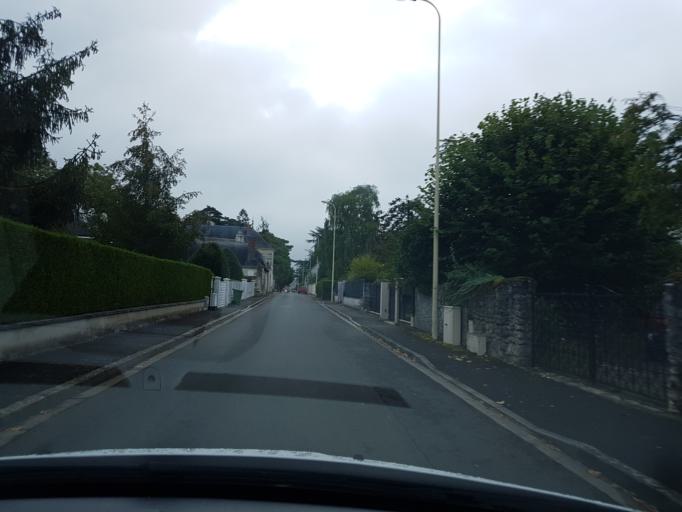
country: FR
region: Centre
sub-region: Departement d'Indre-et-Loire
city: Saint-Avertin
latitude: 47.3670
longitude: 0.7352
